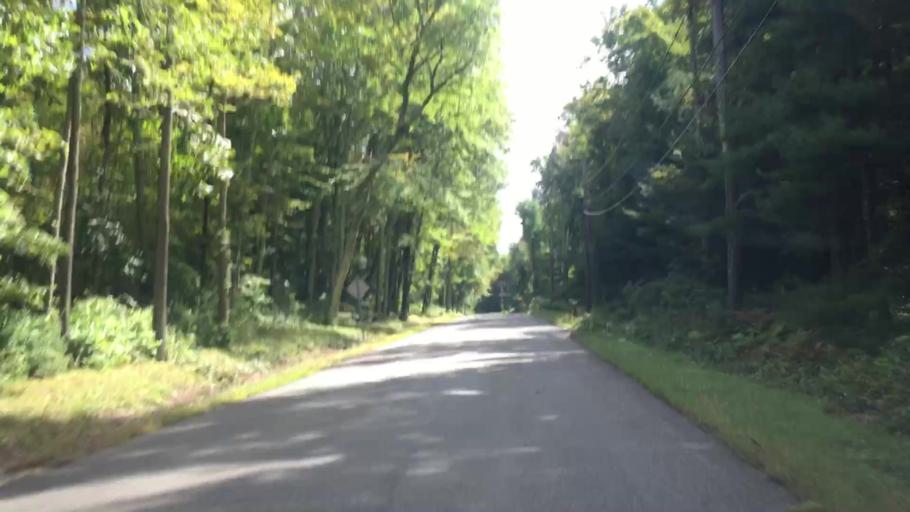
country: US
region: Connecticut
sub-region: Tolland County
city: Stafford Springs
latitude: 41.9187
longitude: -72.2145
